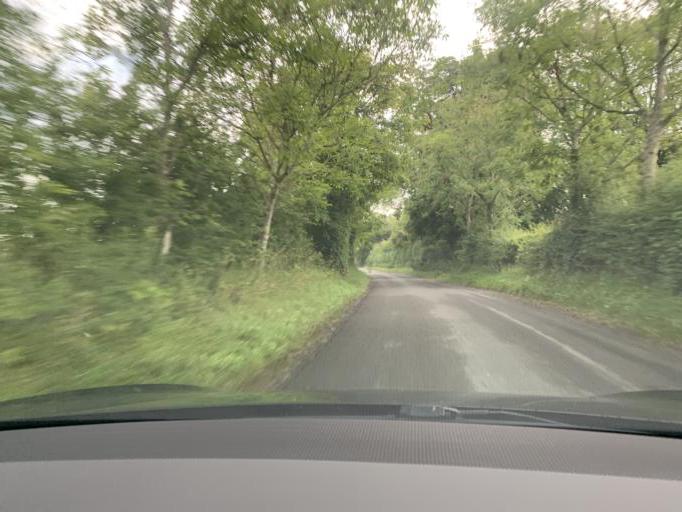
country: GB
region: England
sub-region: Wiltshire
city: Collingbourne Kingston
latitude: 51.2779
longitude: -1.6400
